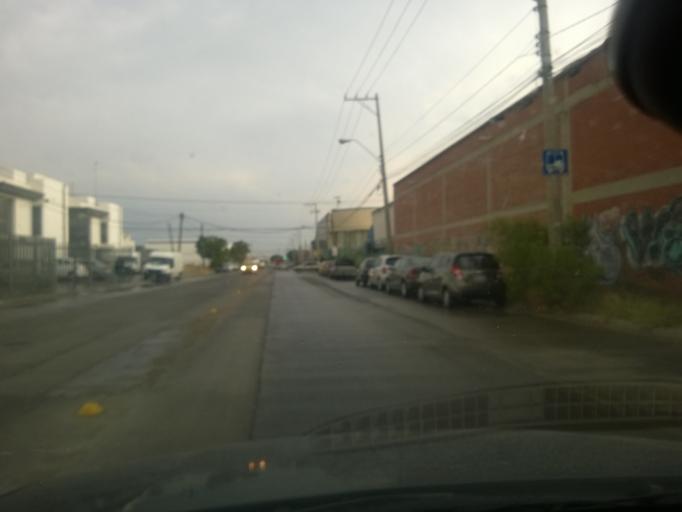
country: MX
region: Guanajuato
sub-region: Leon
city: Fraccionamiento Paraiso Real
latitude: 21.0852
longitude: -101.6222
